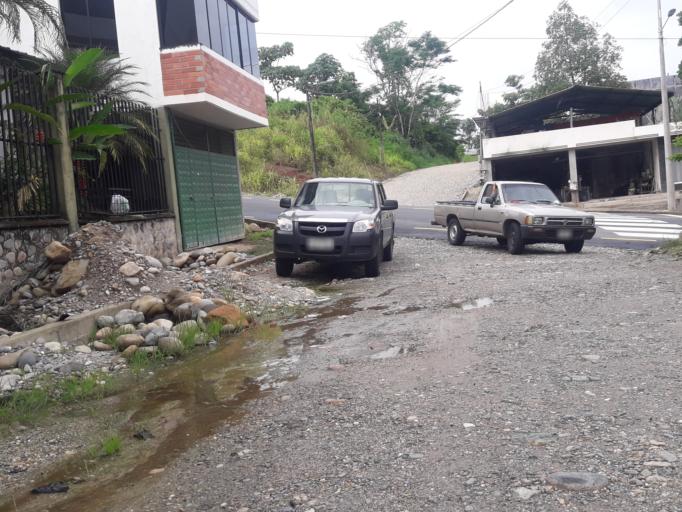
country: EC
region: Napo
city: Tena
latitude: -0.9989
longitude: -77.8080
